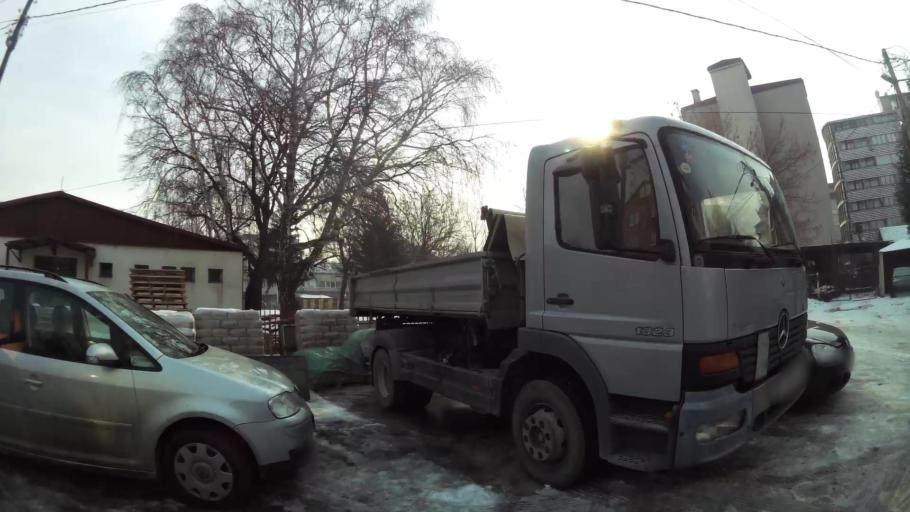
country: MK
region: Cair
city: Cair
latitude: 42.0147
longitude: 21.4429
